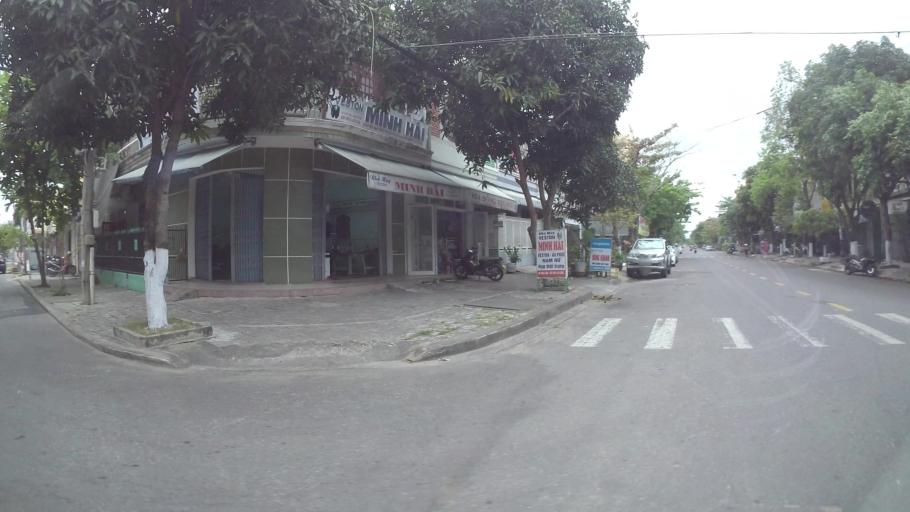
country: VN
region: Da Nang
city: Da Nang
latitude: 16.0865
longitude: 108.2394
